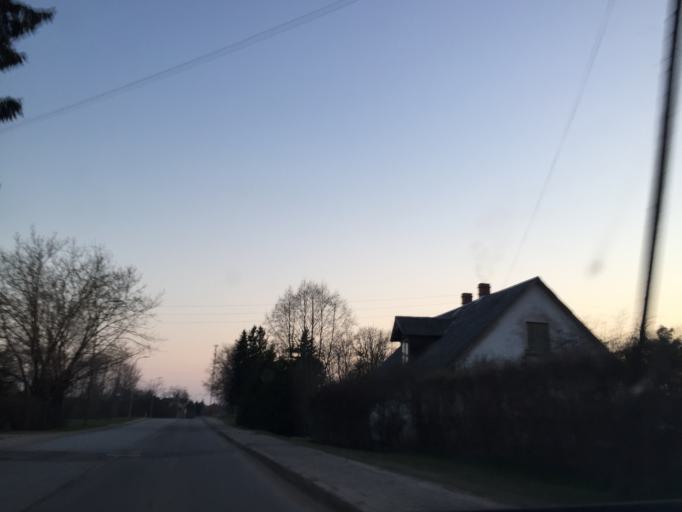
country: LV
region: Valkas Rajons
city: Valka
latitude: 57.7684
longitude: 26.0101
